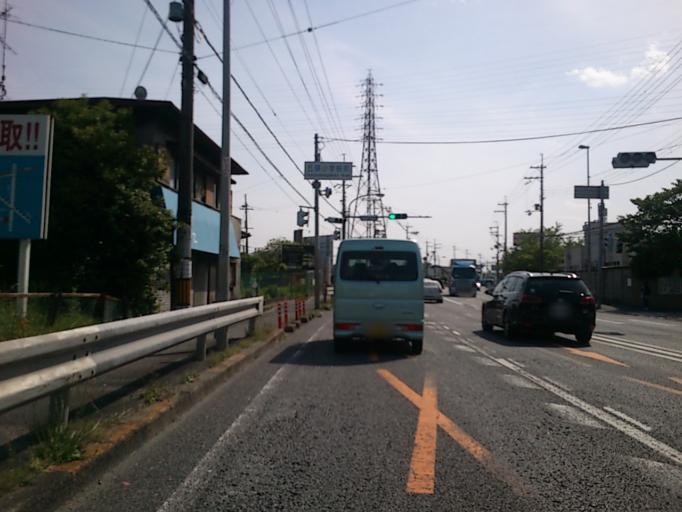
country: JP
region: Osaka
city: Takatsuki
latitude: 34.8617
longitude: 135.6536
